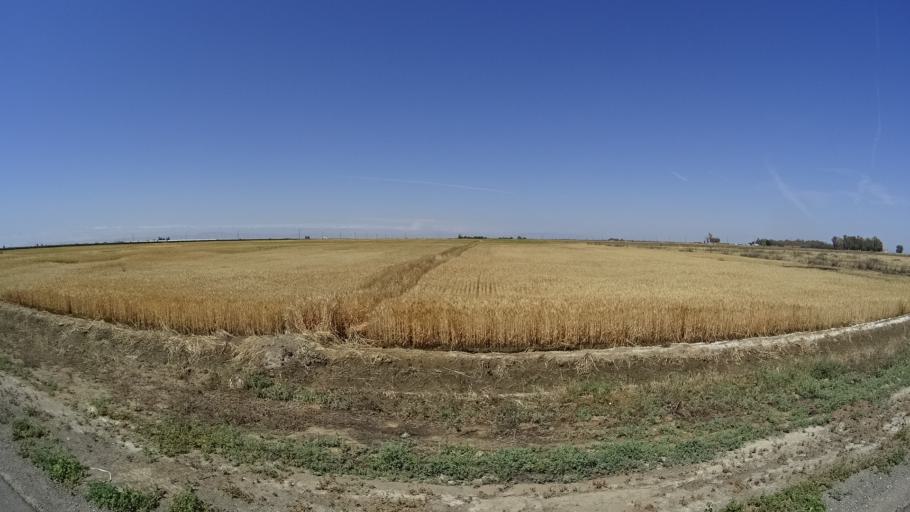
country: US
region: California
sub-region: Kings County
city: Stratford
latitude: 36.2364
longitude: -119.7986
